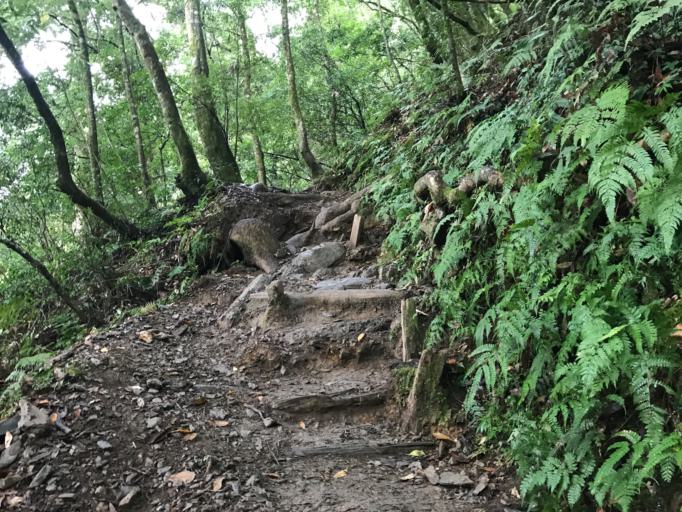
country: TW
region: Taiwan
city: Daxi
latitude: 24.5463
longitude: 121.2915
